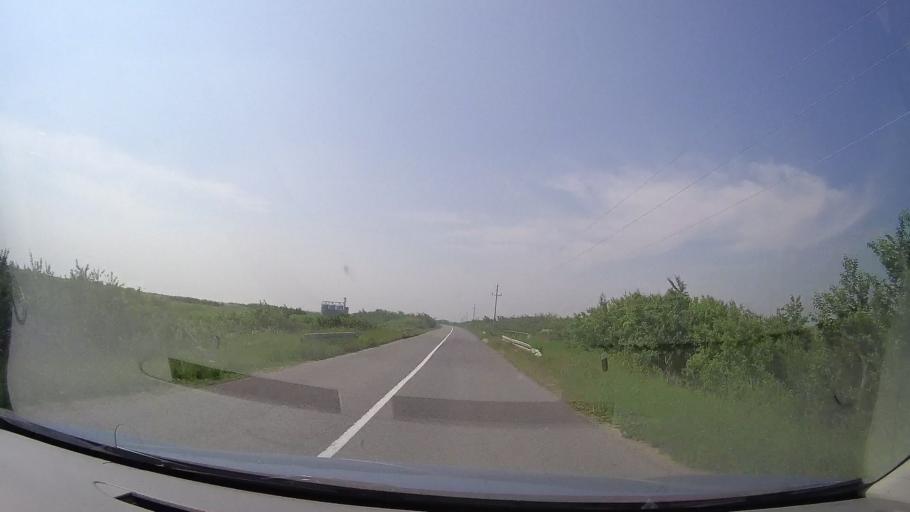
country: RS
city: Jarkovac
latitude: 45.2593
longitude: 20.7637
